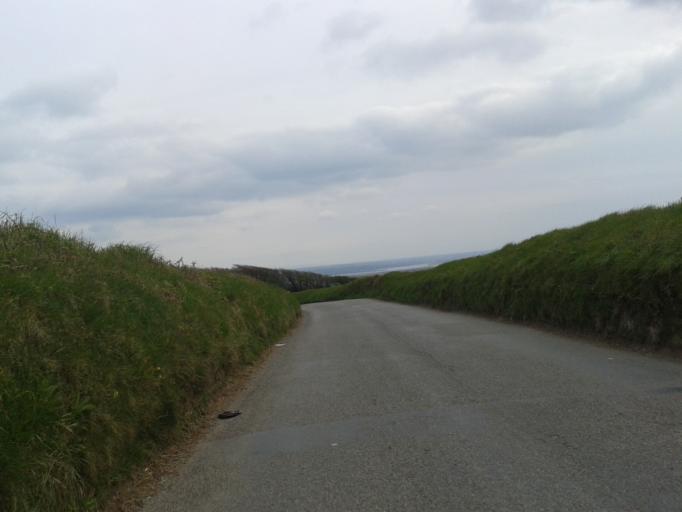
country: GB
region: England
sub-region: Devon
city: Braunton
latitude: 51.1477
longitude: -4.1911
